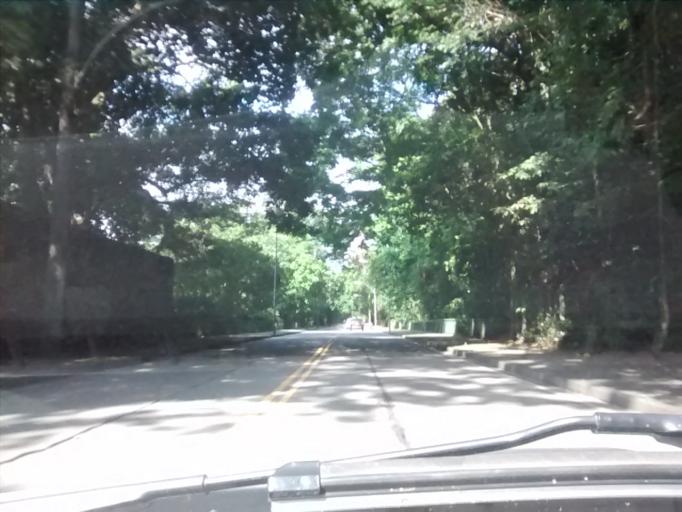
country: BR
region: Rio de Janeiro
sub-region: Rio De Janeiro
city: Rio de Janeiro
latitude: -22.9529
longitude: -43.2610
